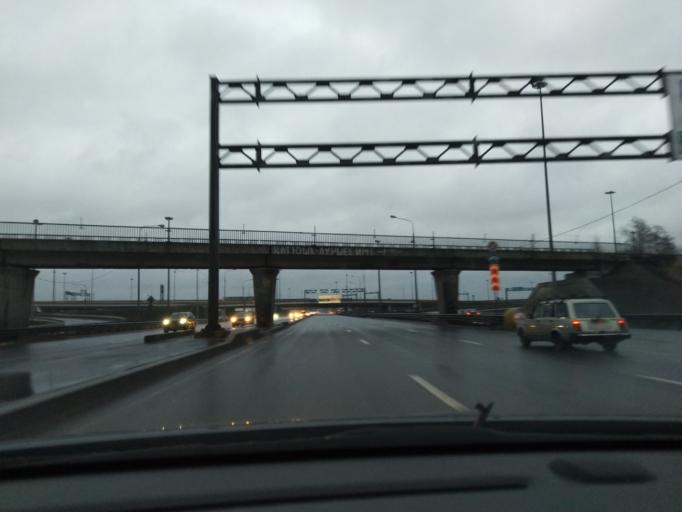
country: RU
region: St.-Petersburg
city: Sosnovaya Polyana
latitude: 59.7968
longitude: 30.1531
